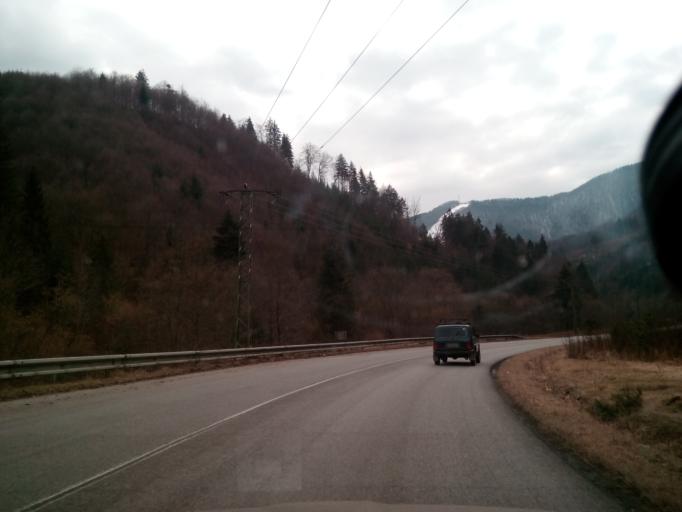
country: SK
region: Zilinsky
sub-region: Okres Zilina
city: Terchova
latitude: 49.2245
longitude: 19.1640
